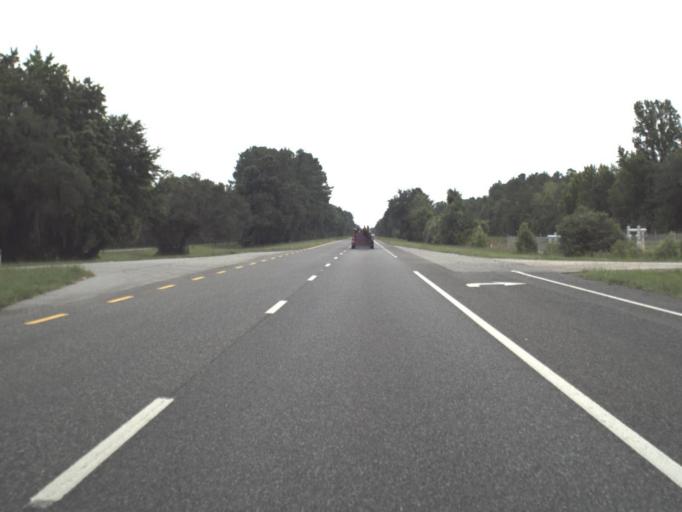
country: US
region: Florida
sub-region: Levy County
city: Bronson
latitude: 29.2789
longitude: -82.7388
